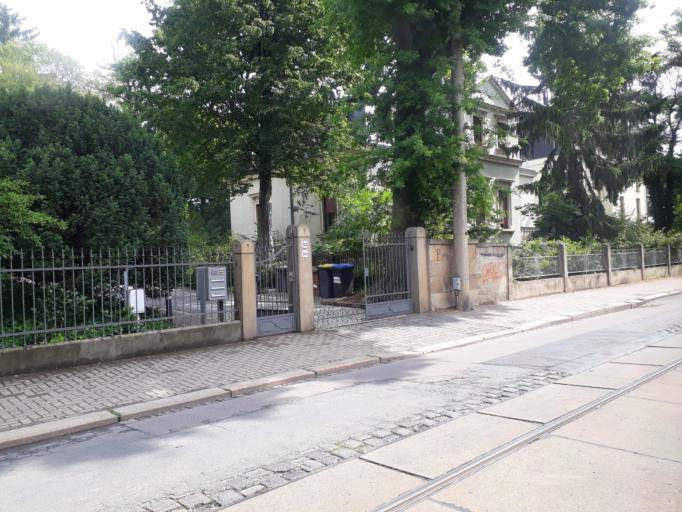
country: DE
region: Saxony
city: Albertstadt
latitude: 51.0531
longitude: 13.7979
